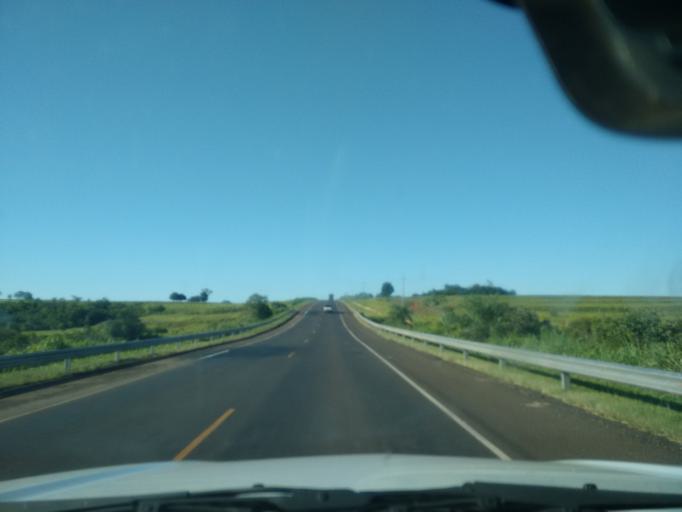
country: PY
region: Canindeyu
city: Salto del Guaira
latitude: -23.9808
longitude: -54.3310
